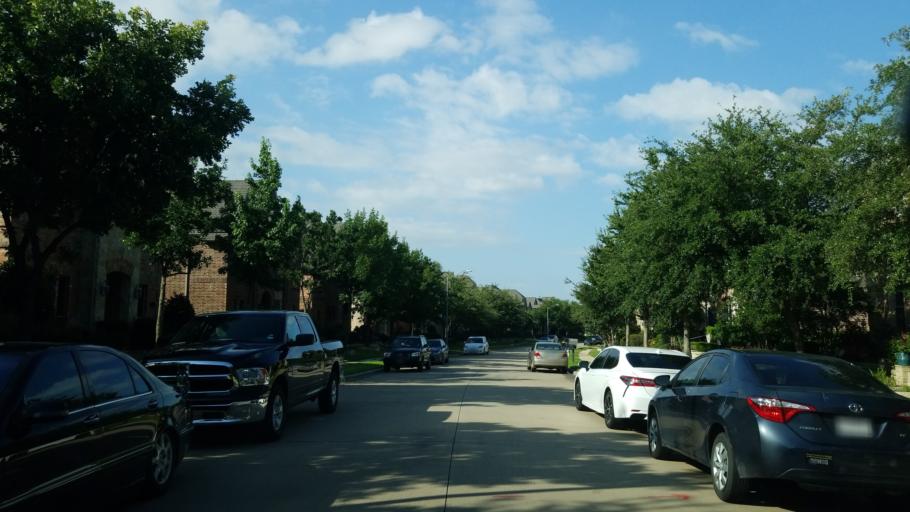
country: US
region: Texas
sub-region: Dallas County
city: Coppell
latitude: 32.9242
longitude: -96.9711
